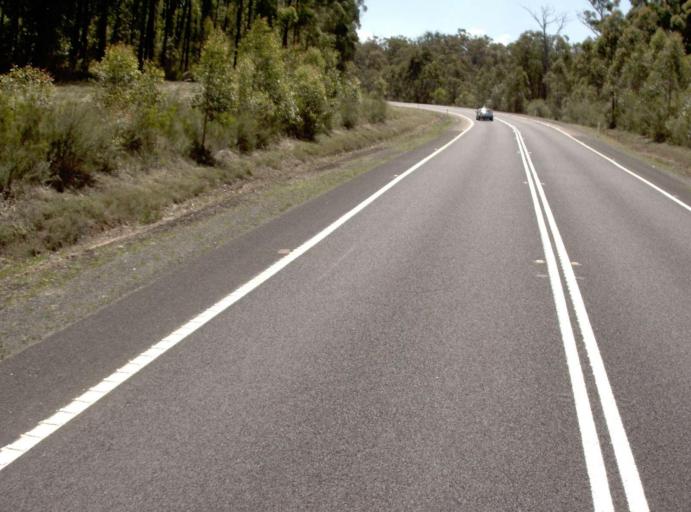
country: AU
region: New South Wales
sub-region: Bombala
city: Bombala
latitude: -37.5659
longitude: 149.1238
